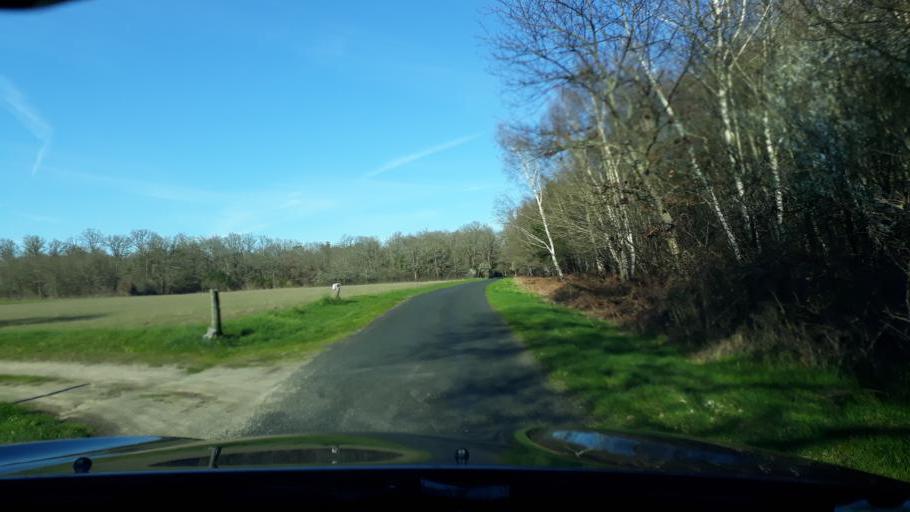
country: FR
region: Centre
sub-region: Departement du Loiret
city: Ligny-le-Ribault
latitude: 47.6902
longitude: 1.7926
